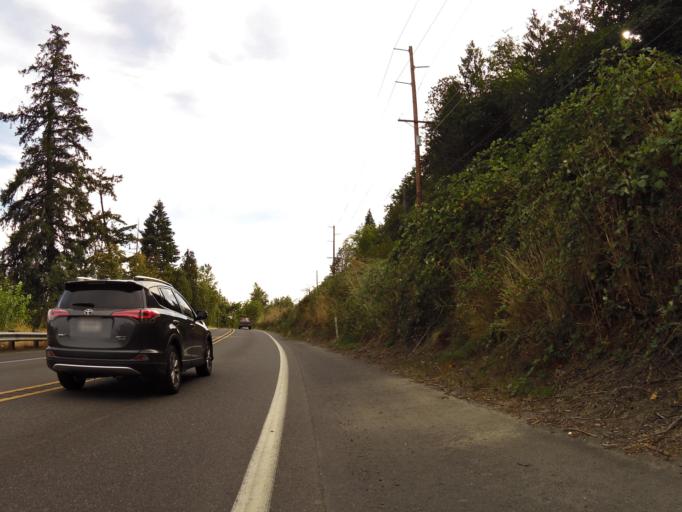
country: US
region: Washington
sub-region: Cowlitz County
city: West Side Highway
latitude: 46.1744
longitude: -122.9146
